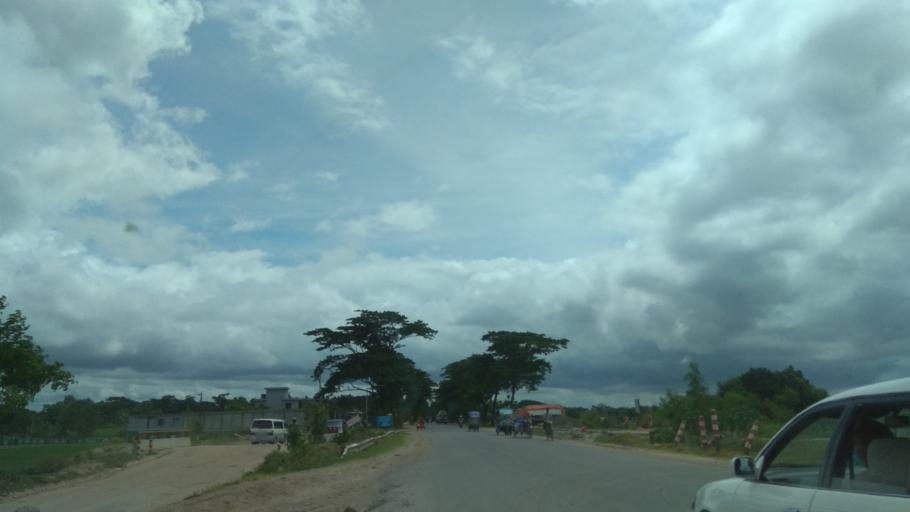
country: BD
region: Khulna
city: Kalia
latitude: 23.2173
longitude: 89.7180
